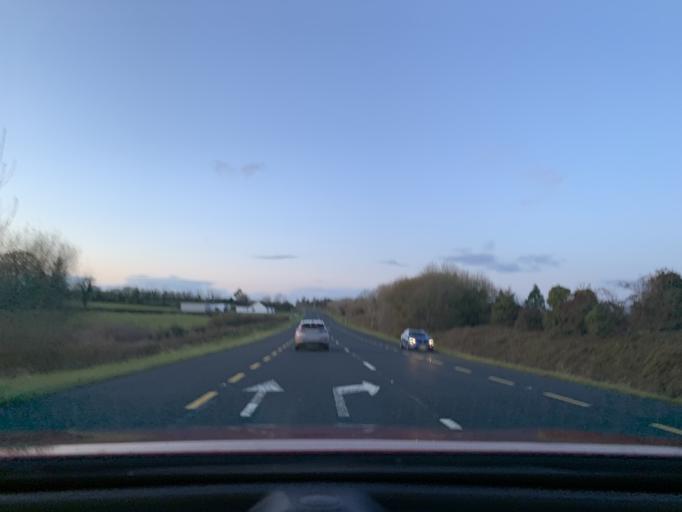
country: IE
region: Connaught
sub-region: County Leitrim
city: Carrick-on-Shannon
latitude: 53.8880
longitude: -7.9438
